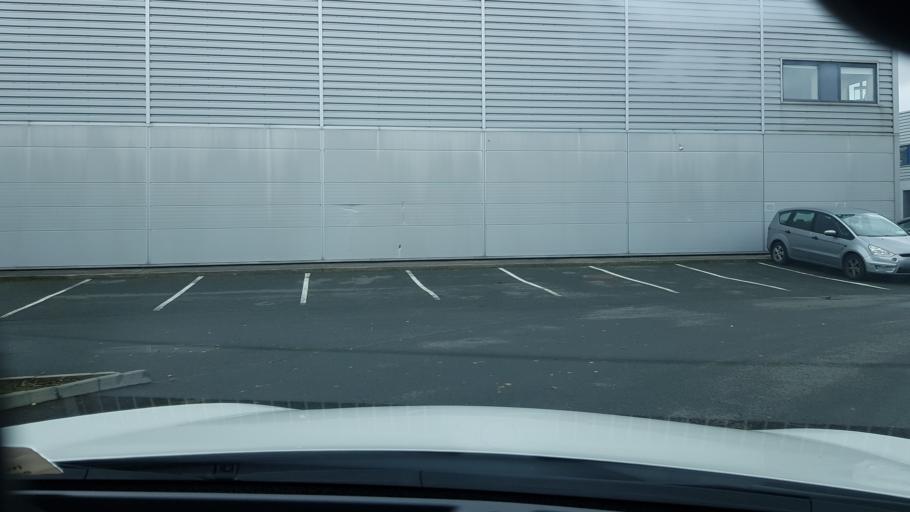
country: IE
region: Leinster
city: Castleknock
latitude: 53.4006
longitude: -6.3451
